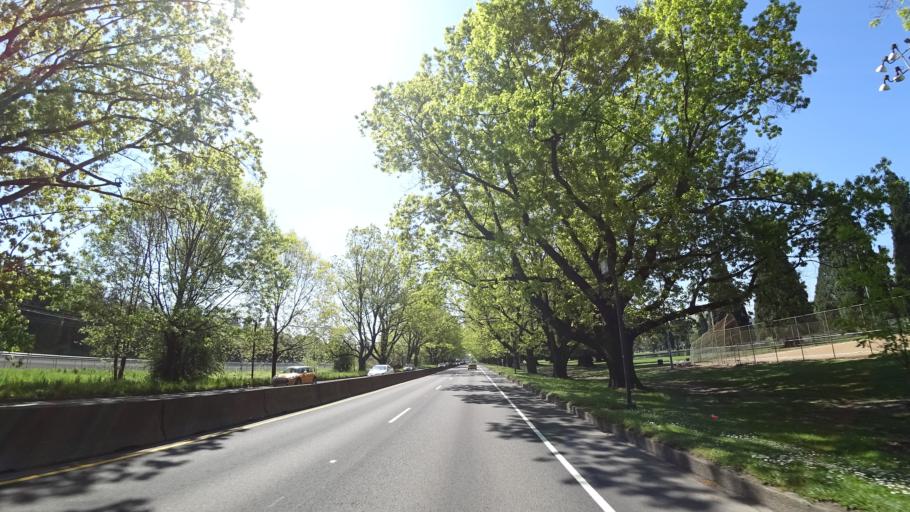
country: US
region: Oregon
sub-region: Clackamas County
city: Milwaukie
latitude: 45.4715
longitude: -122.6399
